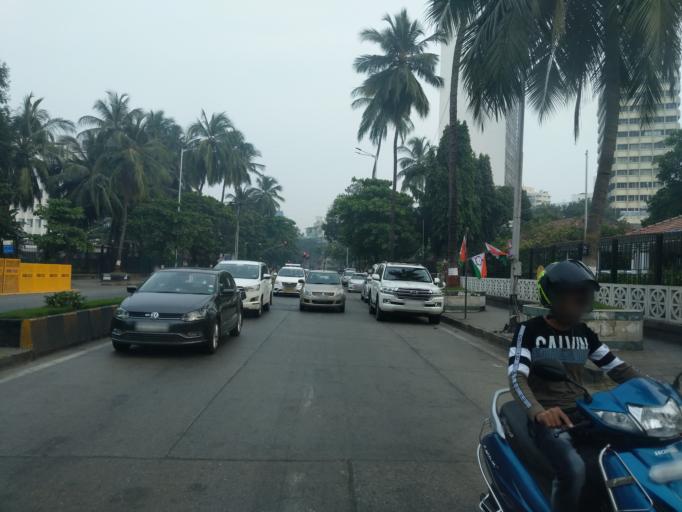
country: IN
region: Maharashtra
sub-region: Raigarh
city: Uran
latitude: 18.9276
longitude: 72.8252
